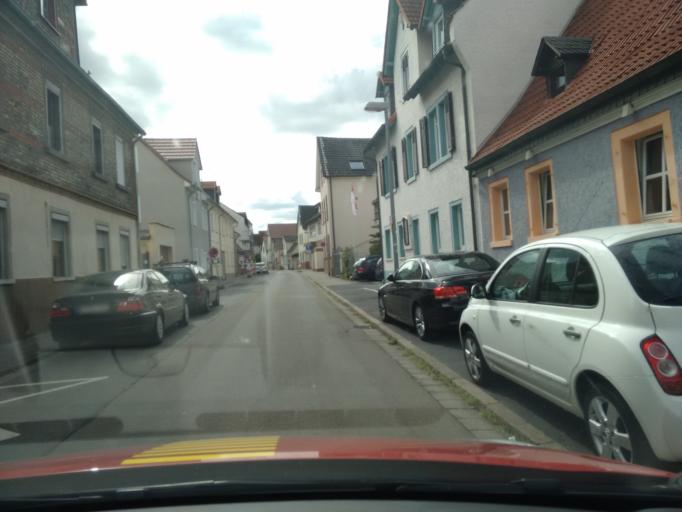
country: DE
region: Rheinland-Pfalz
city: Budenheim
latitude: 50.0004
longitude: 8.2097
